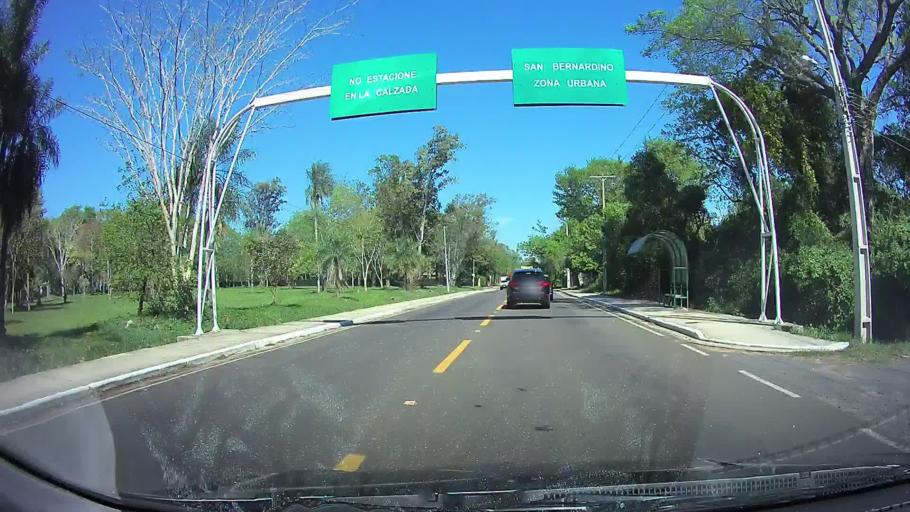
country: PY
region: Cordillera
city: San Bernardino
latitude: -25.2879
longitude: -57.3132
